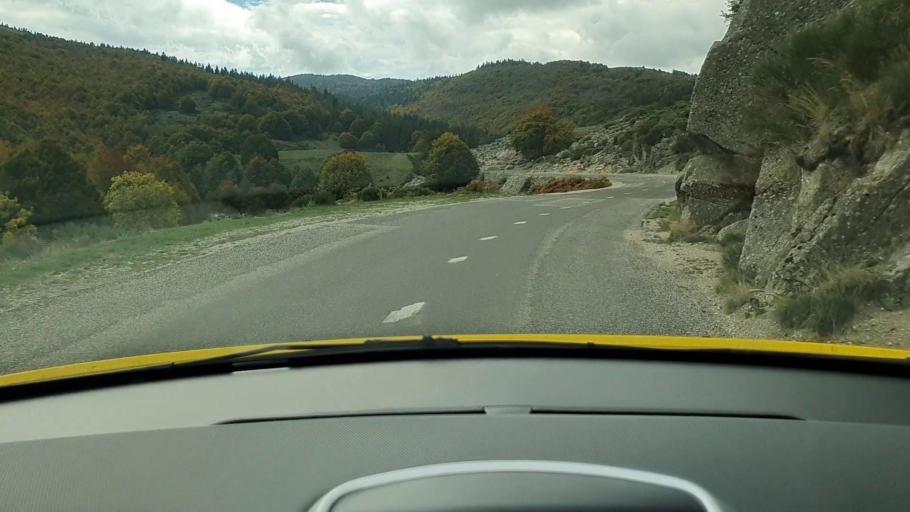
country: FR
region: Languedoc-Roussillon
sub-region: Departement de la Lozere
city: Meyrueis
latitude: 44.0750
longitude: 3.5001
